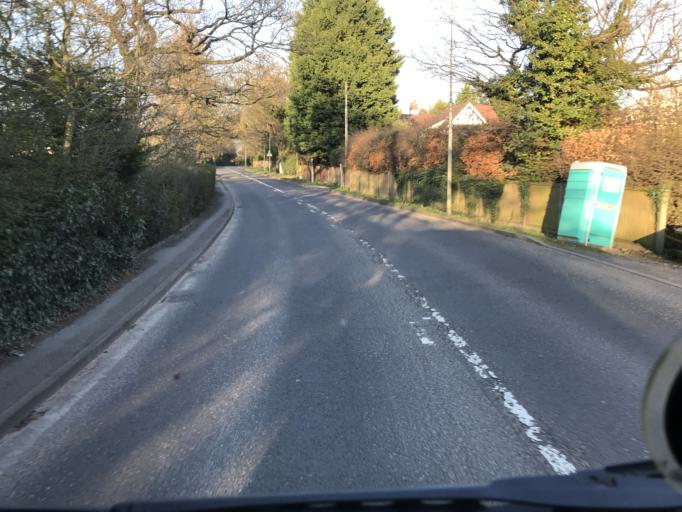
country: GB
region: England
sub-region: Cheshire East
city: Wilmslow
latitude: 53.3283
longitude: -2.2043
